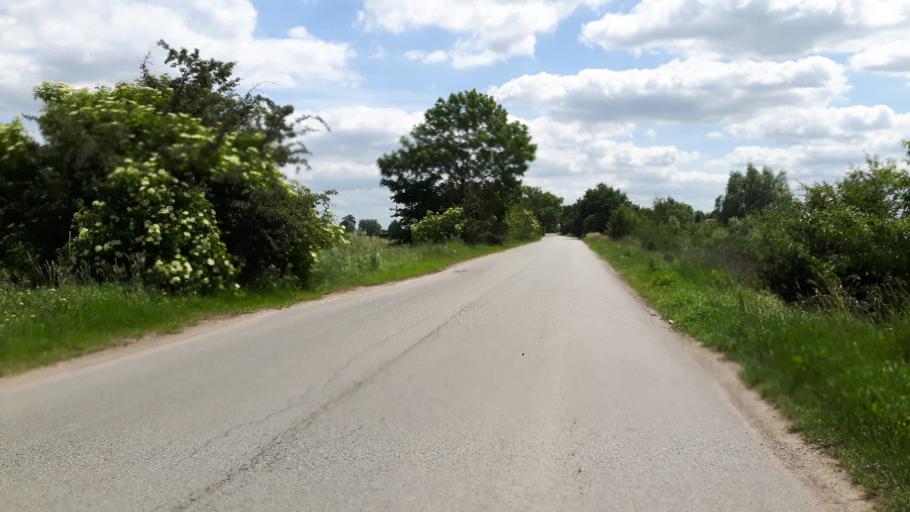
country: PL
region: Pomeranian Voivodeship
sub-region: Powiat gdanski
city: Cedry Wielkie
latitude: 54.3376
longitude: 18.8042
